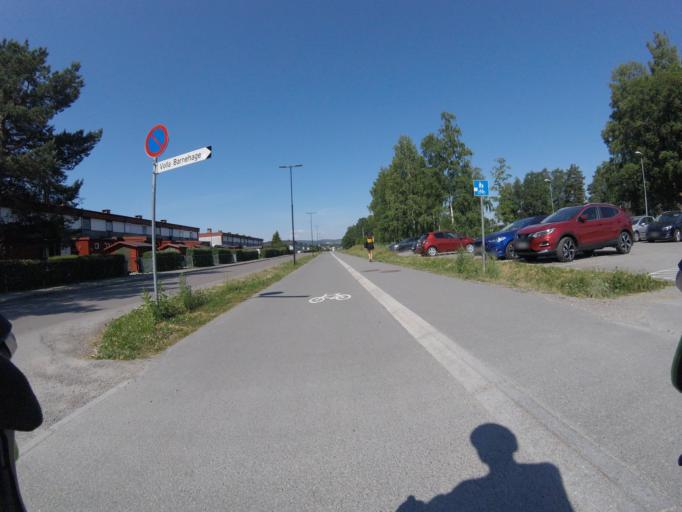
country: NO
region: Akershus
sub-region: Skedsmo
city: Lillestrom
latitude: 59.9637
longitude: 11.0460
